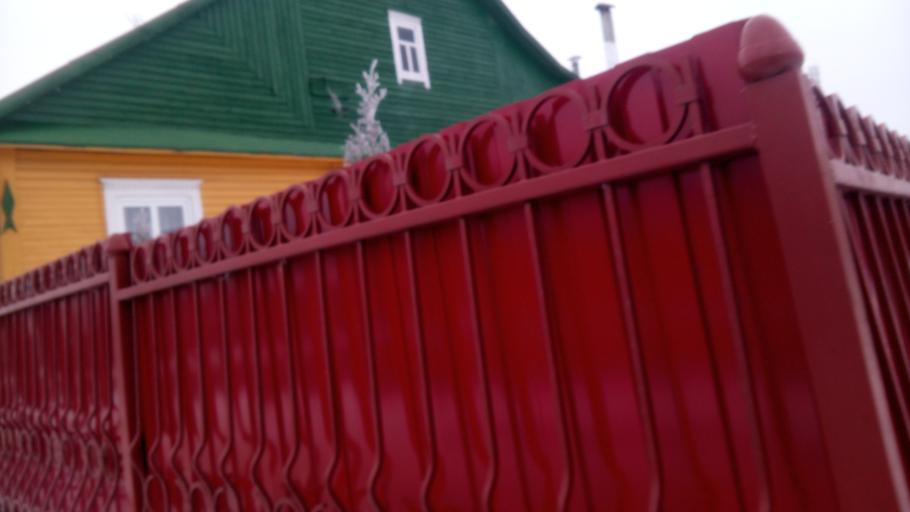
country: BY
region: Grodnenskaya
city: Slonim
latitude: 53.0851
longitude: 25.3226
